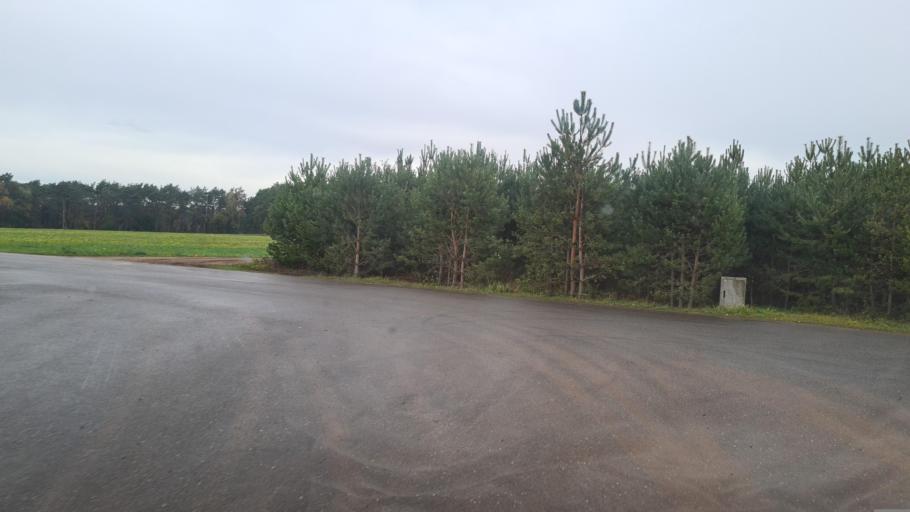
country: DE
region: Saxony-Anhalt
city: Abtsdorf
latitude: 51.9156
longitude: 12.6993
